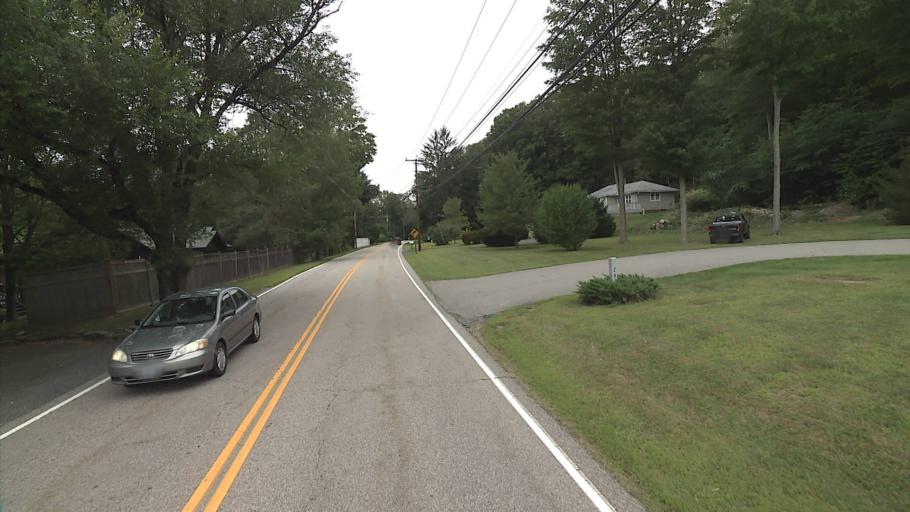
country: US
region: Connecticut
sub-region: Middlesex County
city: Essex Village
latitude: 41.3911
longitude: -72.3510
